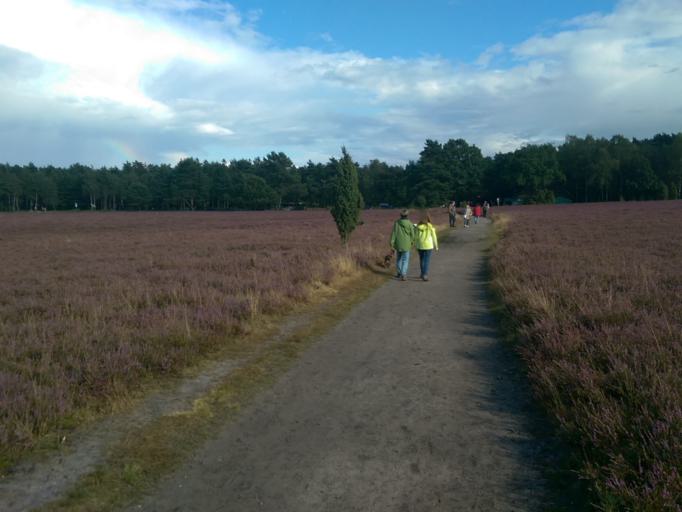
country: DE
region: Lower Saxony
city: Schneverdingen
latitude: 53.1372
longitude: 9.8042
